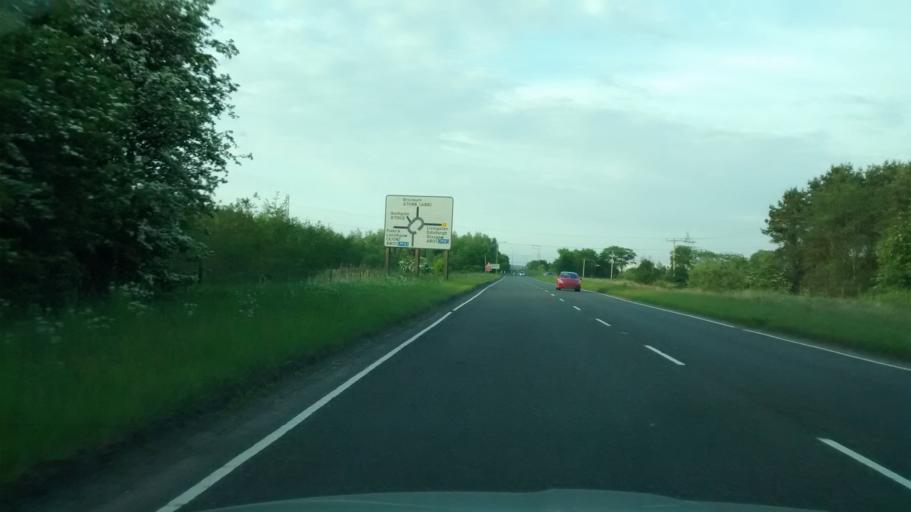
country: GB
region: Scotland
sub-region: West Lothian
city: Whitburn
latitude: 55.8785
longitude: -3.6662
